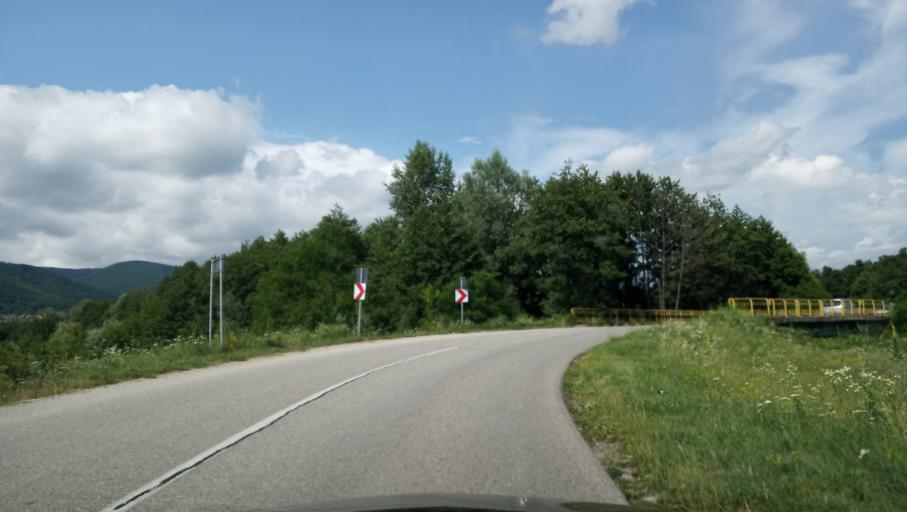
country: RO
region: Gorj
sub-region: Comuna Musetesti
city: Musetesti
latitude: 45.1584
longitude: 23.4626
